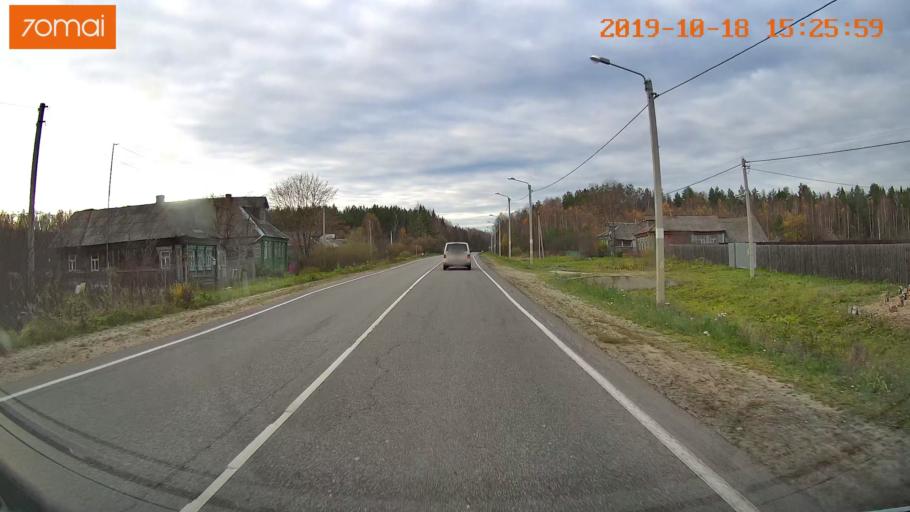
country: RU
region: Vladimir
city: Anopino
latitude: 55.7432
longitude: 40.6953
